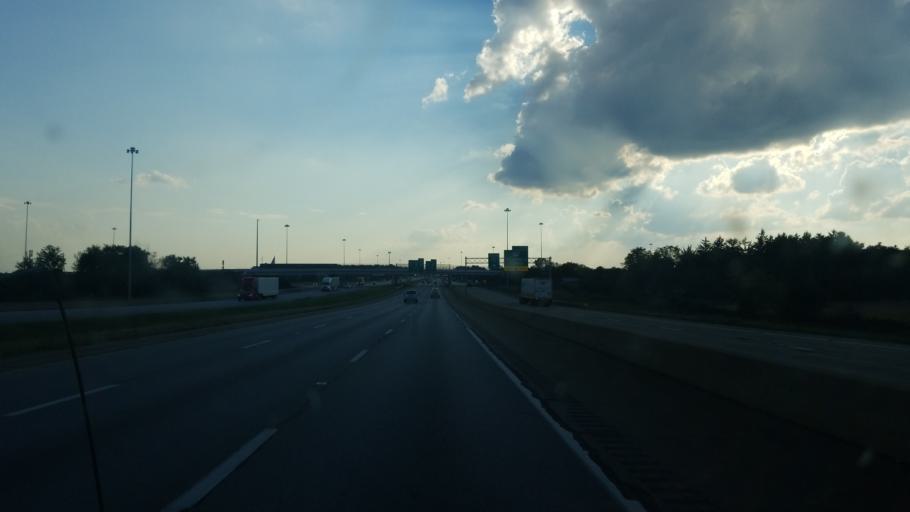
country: US
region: Ohio
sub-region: Wood County
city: Perrysburg
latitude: 41.5673
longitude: -83.5836
